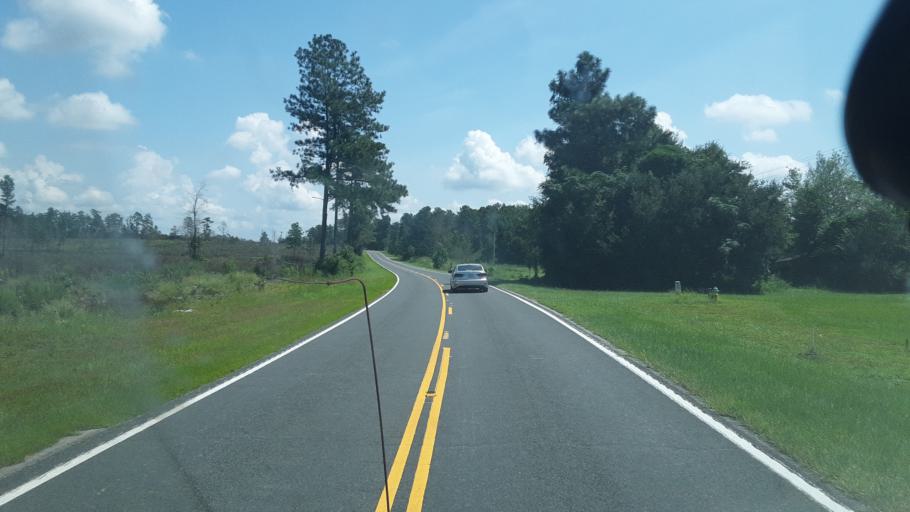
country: US
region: South Carolina
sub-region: Calhoun County
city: Oak Grove
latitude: 33.6348
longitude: -81.0115
